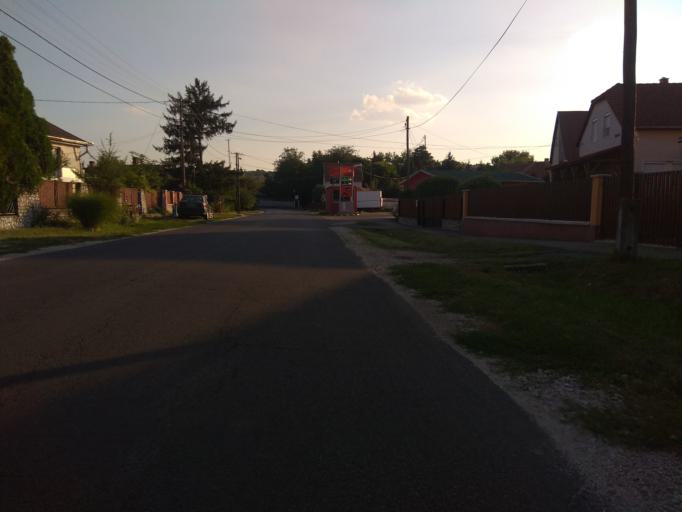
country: HU
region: Borsod-Abauj-Zemplen
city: Nyekladhaza
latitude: 47.9893
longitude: 20.8348
